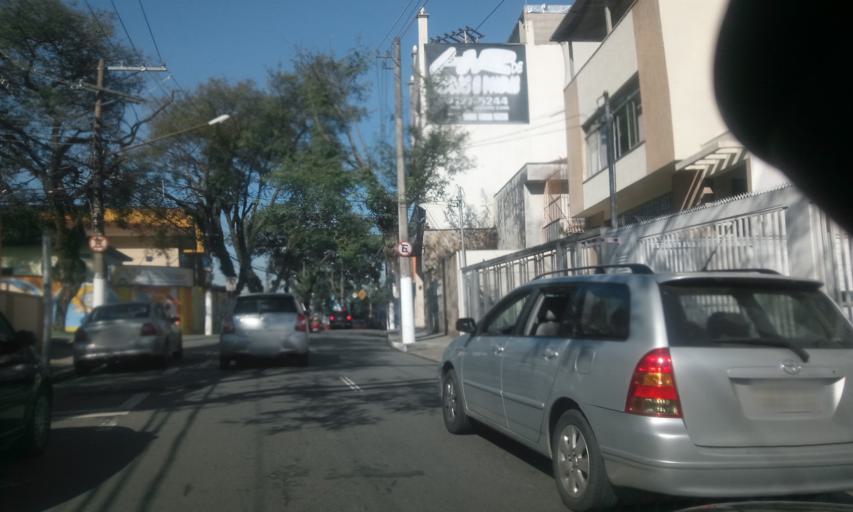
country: BR
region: Sao Paulo
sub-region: Sao Bernardo Do Campo
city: Sao Bernardo do Campo
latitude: -23.7193
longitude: -46.5475
